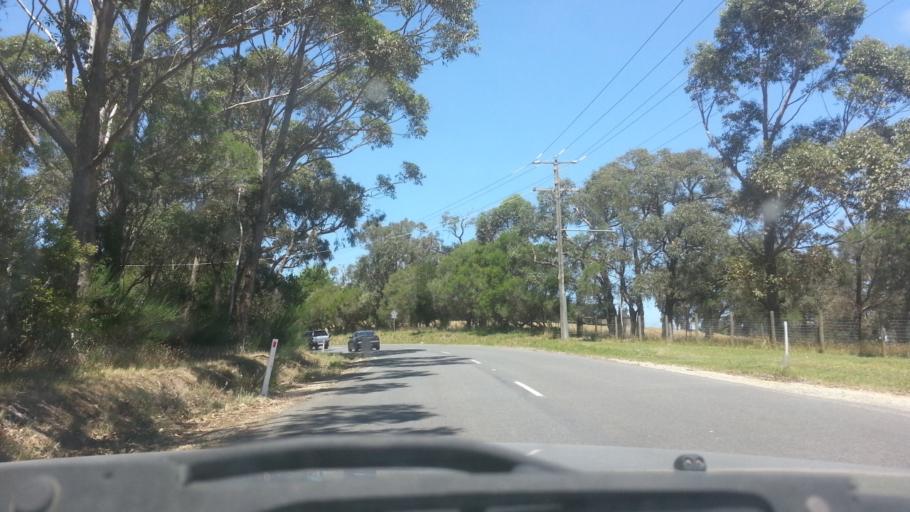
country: AU
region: Victoria
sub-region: Cardinia
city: Beaconsfield Upper
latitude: -37.9793
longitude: 145.3921
